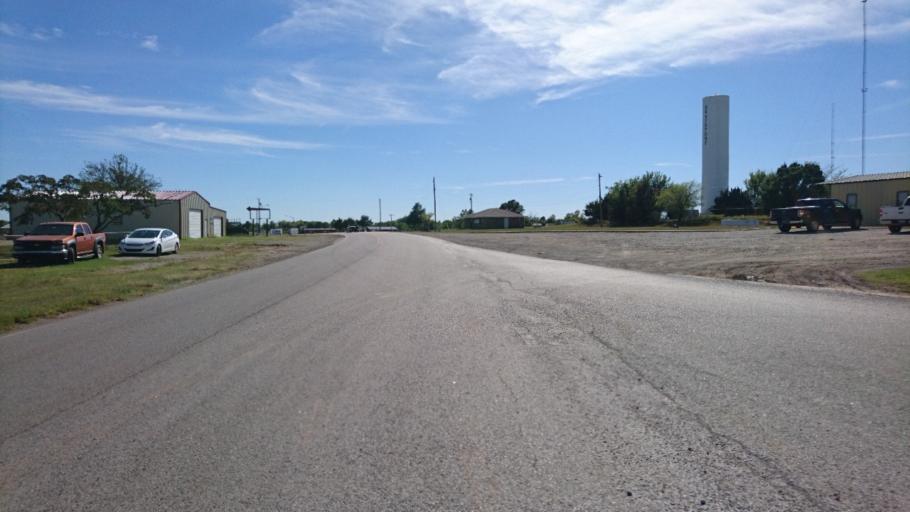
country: US
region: Oklahoma
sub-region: Lincoln County
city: Stroud
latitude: 35.7179
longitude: -96.7647
